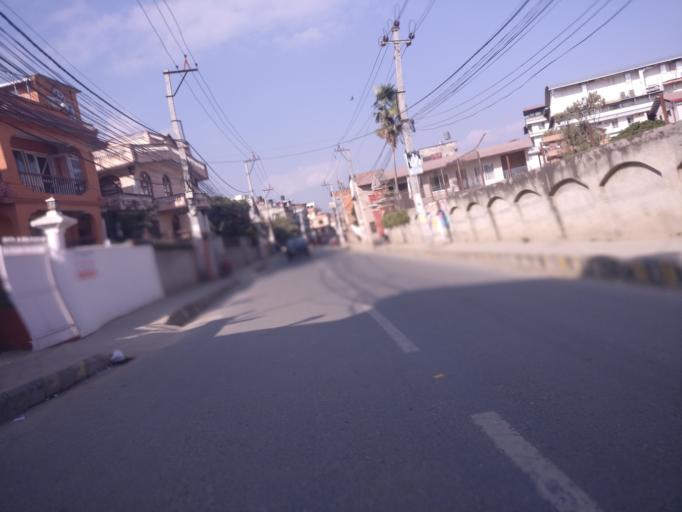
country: NP
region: Central Region
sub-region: Bagmati Zone
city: Patan
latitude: 27.6737
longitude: 85.3079
